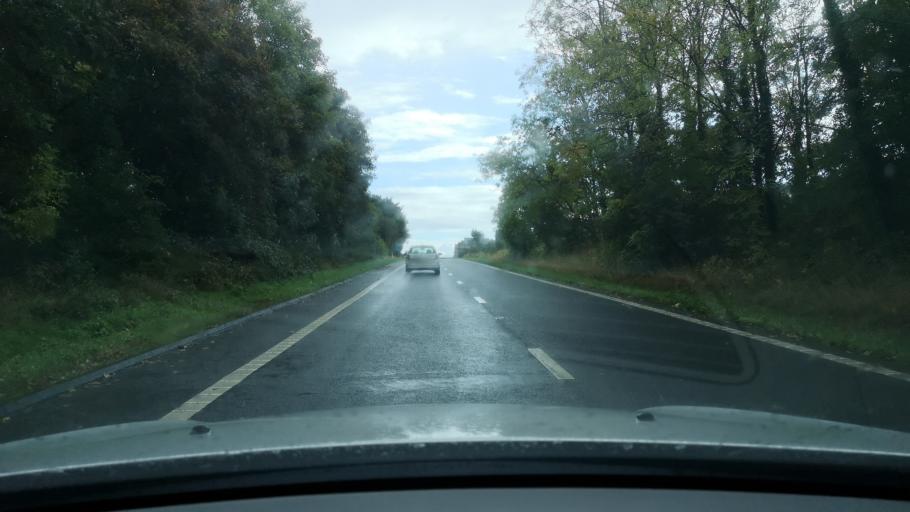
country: GB
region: England
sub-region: City and Borough of Wakefield
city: Knottingley
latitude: 53.6950
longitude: -1.2624
